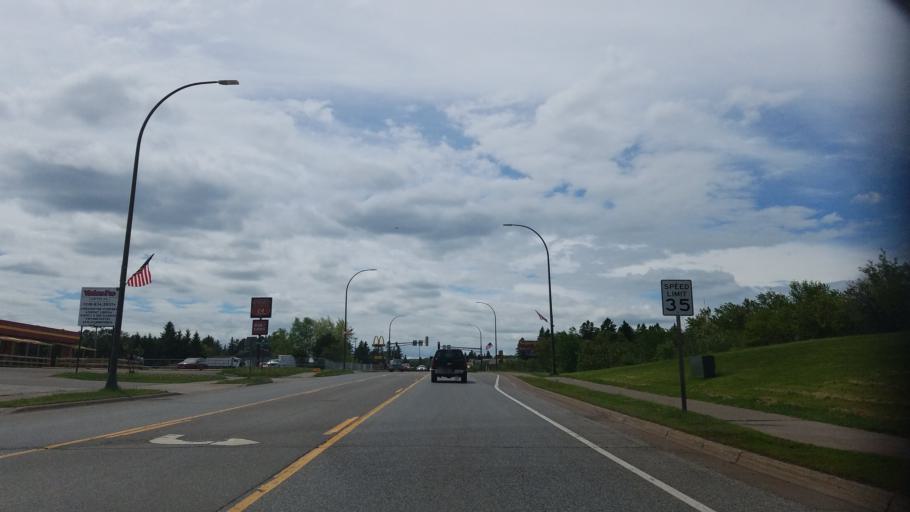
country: US
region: Minnesota
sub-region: Lake County
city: Two Harbors
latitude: 47.0257
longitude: -91.6788
